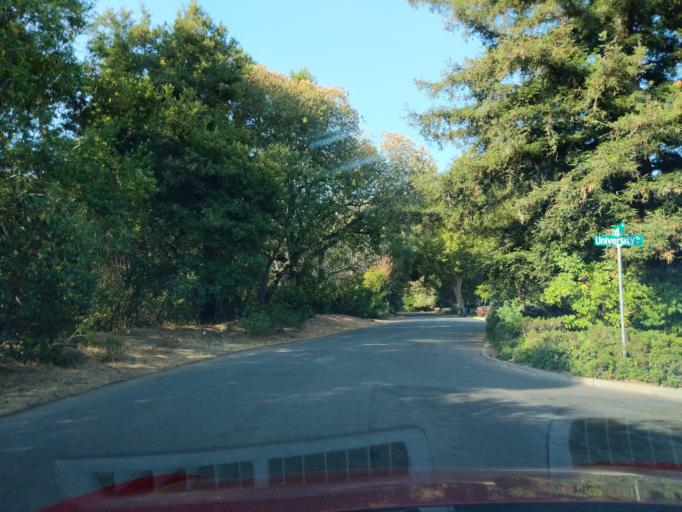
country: US
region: California
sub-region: San Mateo County
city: Menlo Park
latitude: 37.4435
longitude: -122.1751
